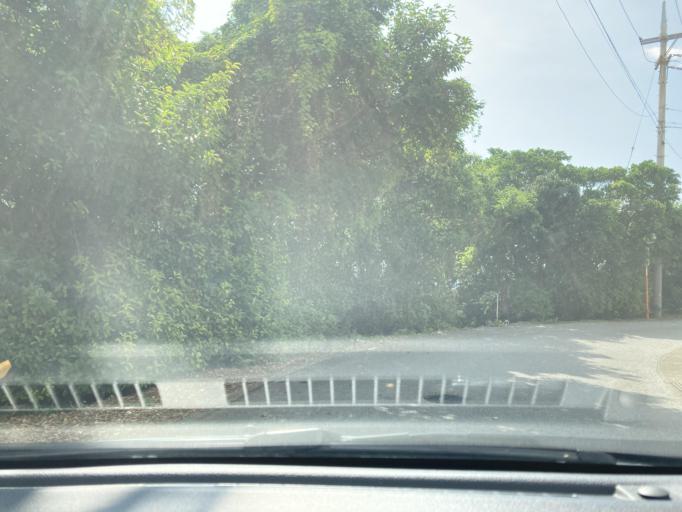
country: JP
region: Okinawa
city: Itoman
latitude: 26.1291
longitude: 127.7755
